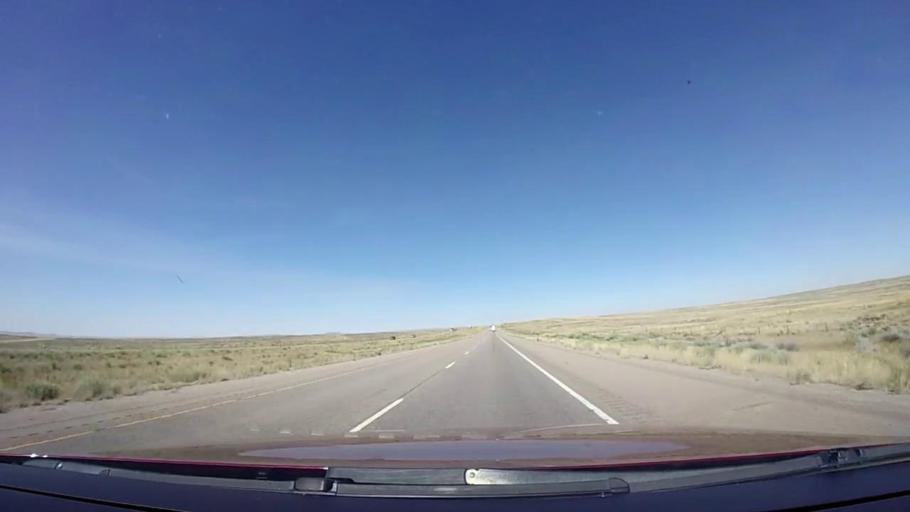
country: US
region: Wyoming
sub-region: Sweetwater County
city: Rock Springs
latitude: 41.6386
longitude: -108.4592
